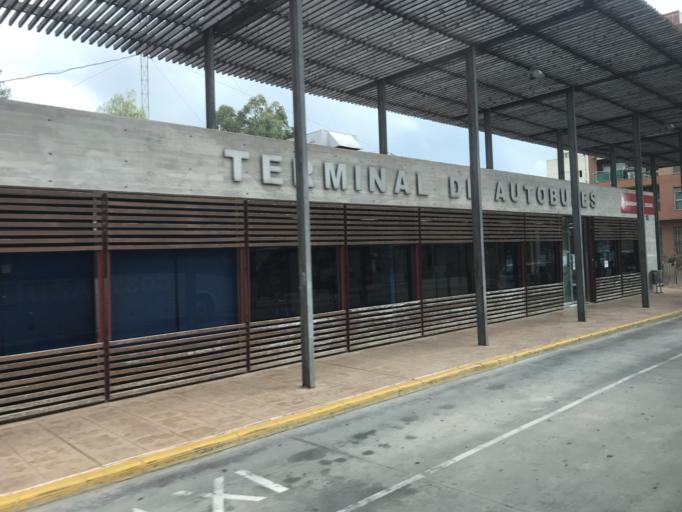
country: ES
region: Valencia
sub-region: Provincia de Alicante
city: Guardamar del Segura
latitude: 38.0878
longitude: -0.6562
